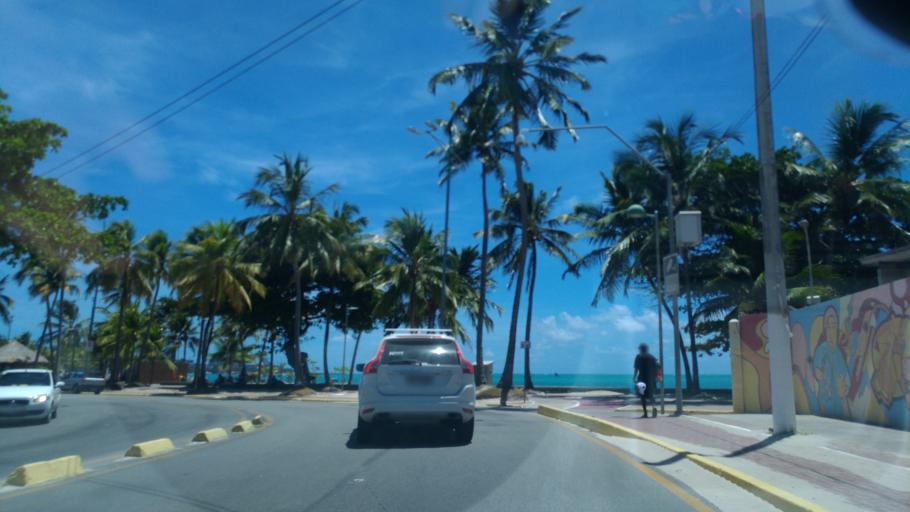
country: BR
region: Alagoas
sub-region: Maceio
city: Maceio
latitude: -9.6743
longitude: -35.7176
